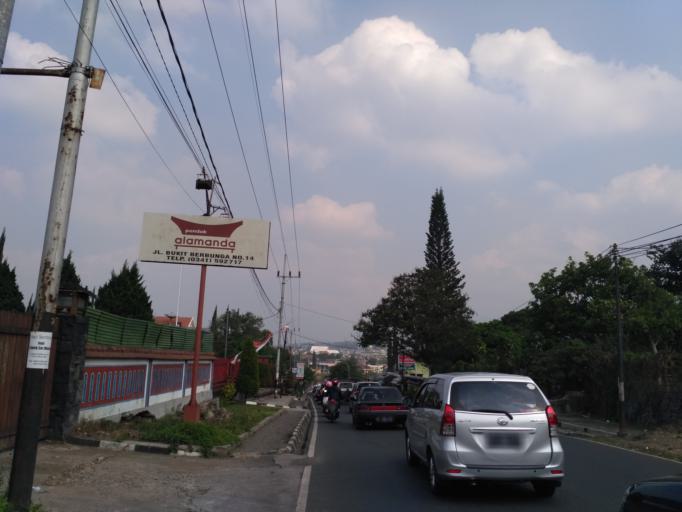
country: ID
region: East Java
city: Batu
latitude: -7.8607
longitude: 112.5268
